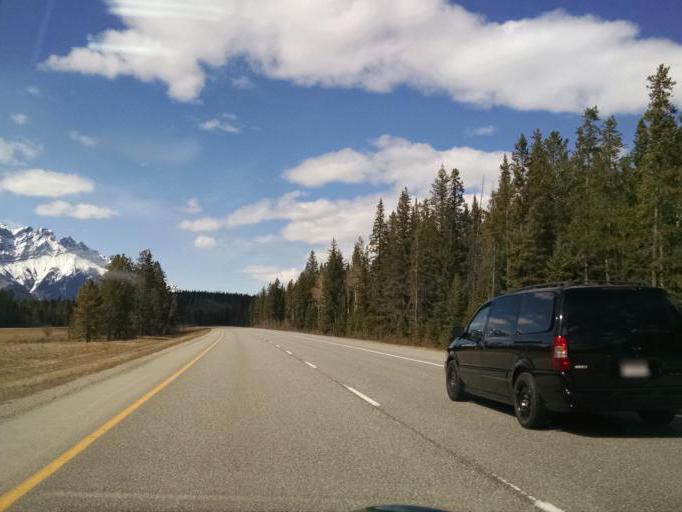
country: CA
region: Alberta
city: Canmore
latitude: 51.1555
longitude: -115.4343
